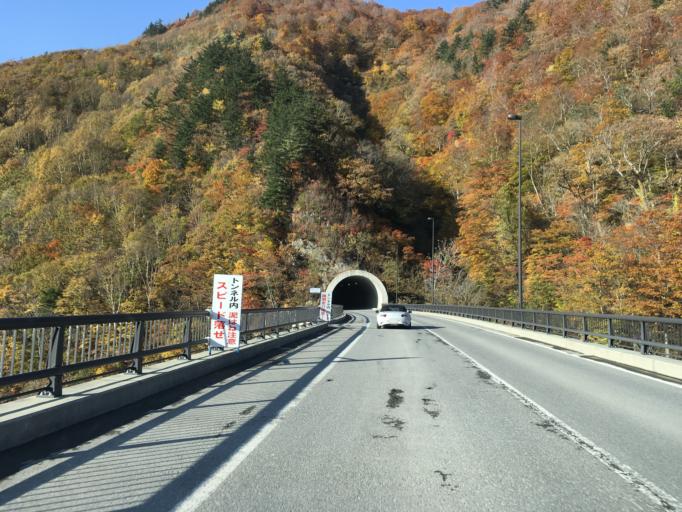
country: JP
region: Akita
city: Yuzawa
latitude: 39.0384
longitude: 140.7349
